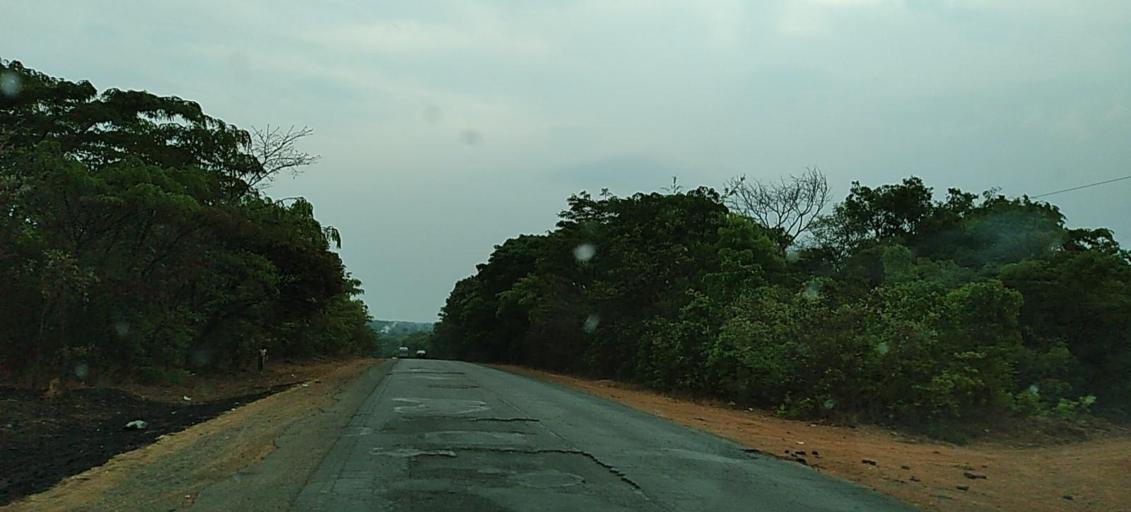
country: ZM
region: Copperbelt
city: Luanshya
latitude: -13.0719
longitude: 28.4501
